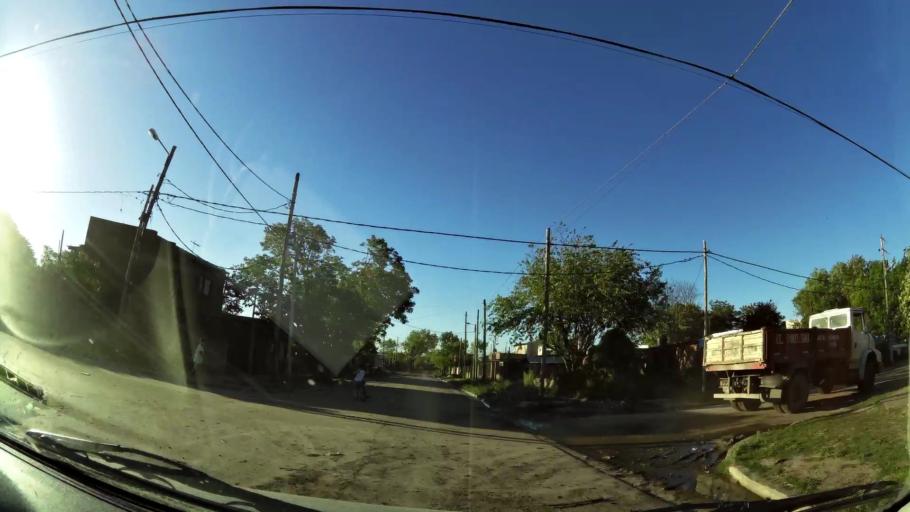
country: AR
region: Buenos Aires
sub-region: Partido de Almirante Brown
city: Adrogue
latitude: -34.7731
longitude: -58.3417
